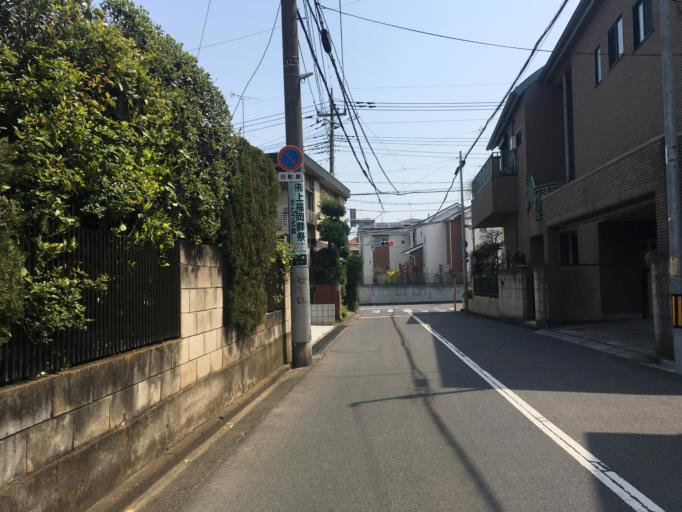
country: JP
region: Saitama
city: Kamifukuoka
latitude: 35.8855
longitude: 139.5213
